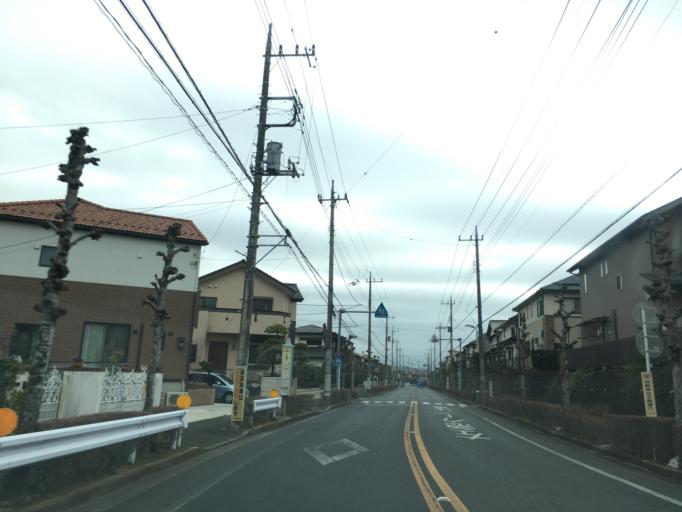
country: JP
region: Tokyo
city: Higashimurayama-shi
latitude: 35.7759
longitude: 139.4607
